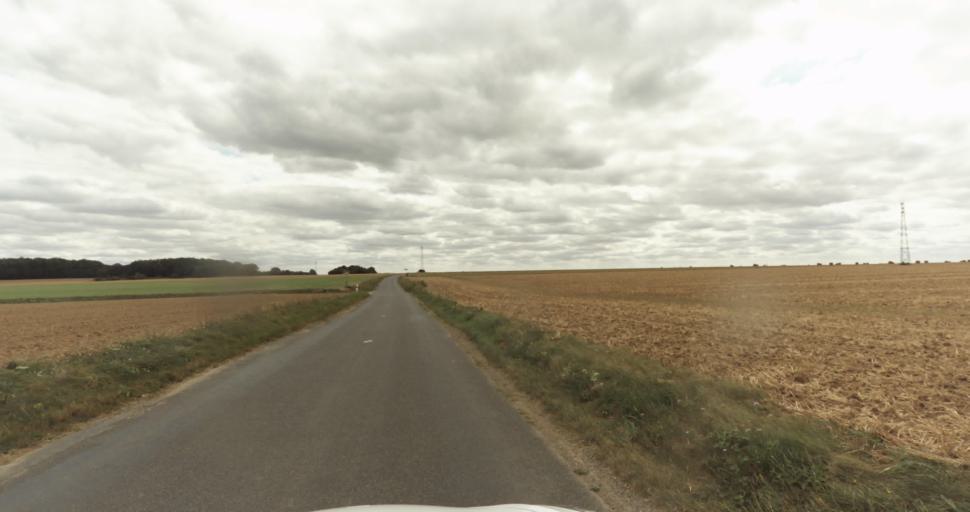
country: FR
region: Centre
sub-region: Departement d'Eure-et-Loir
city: Vert-en-Drouais
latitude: 48.7898
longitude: 1.2864
